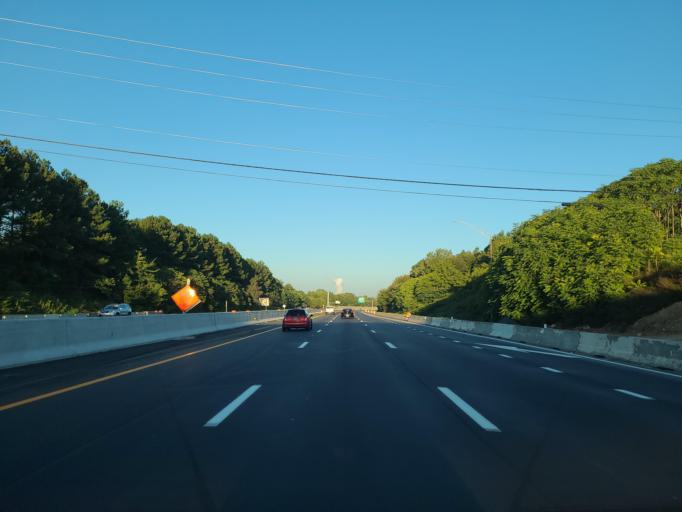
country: US
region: North Carolina
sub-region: Union County
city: Marvin
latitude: 35.0638
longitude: -80.8216
